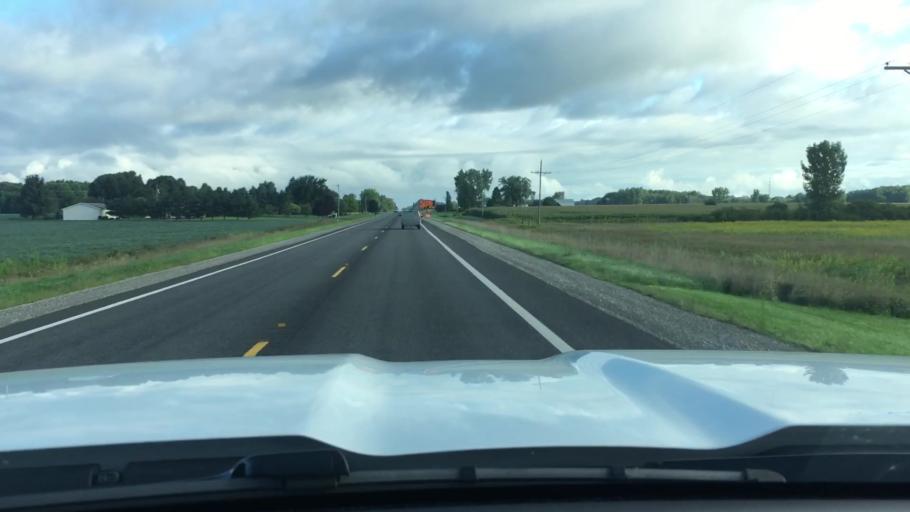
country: US
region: Michigan
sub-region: Tuscola County
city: Caro
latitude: 43.3807
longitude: -83.3833
